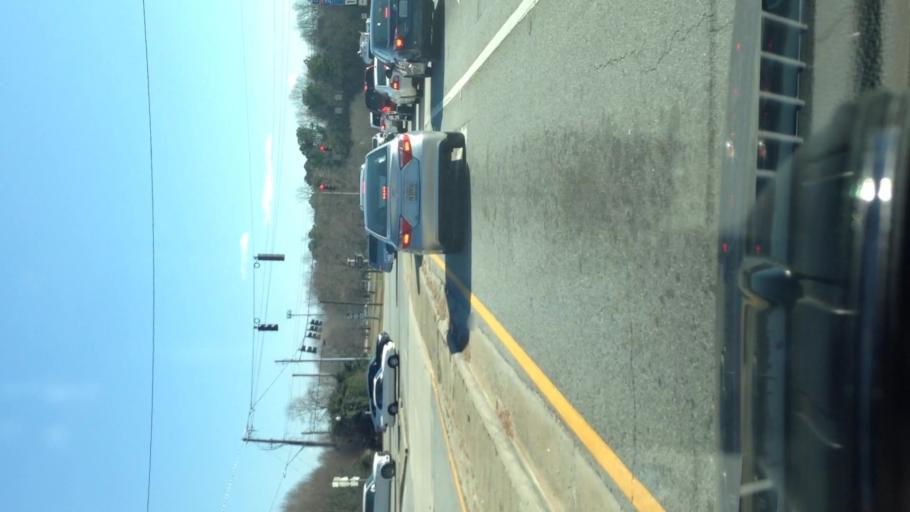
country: US
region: Georgia
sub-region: DeKalb County
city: Doraville
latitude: 33.9030
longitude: -84.2750
